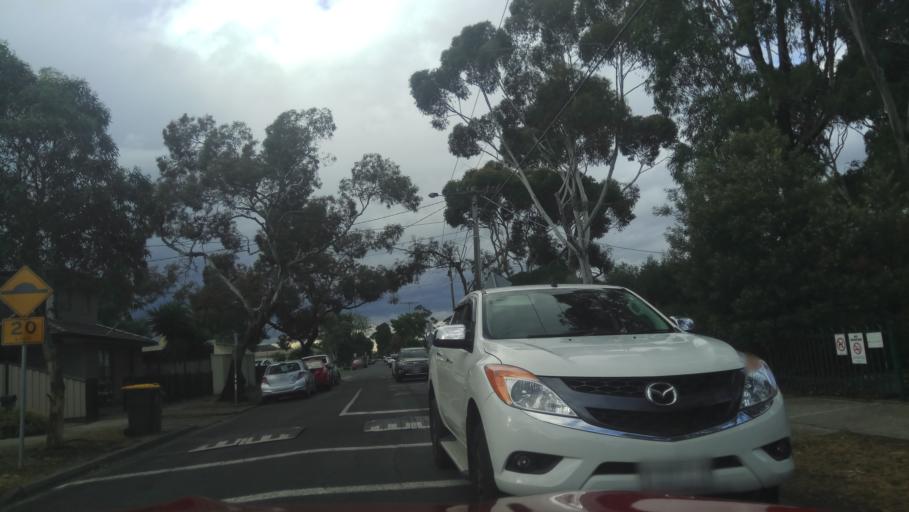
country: AU
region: Victoria
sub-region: Hobsons Bay
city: Altona North
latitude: -37.8374
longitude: 144.8483
